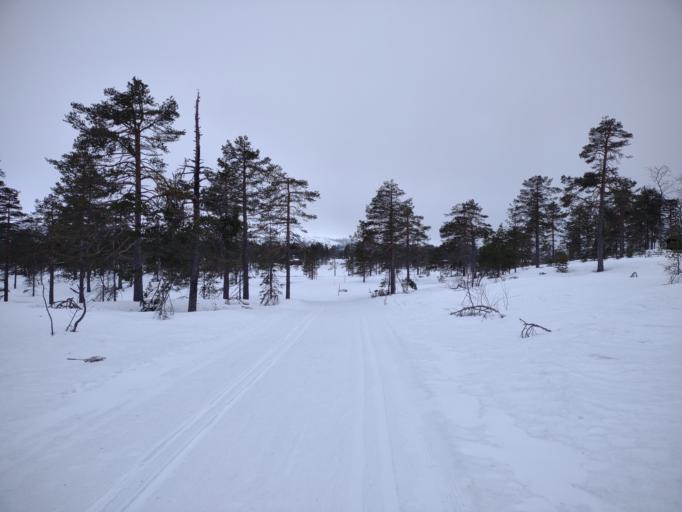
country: NO
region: Buskerud
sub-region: Flesberg
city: Lampeland
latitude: 59.7950
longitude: 9.4388
